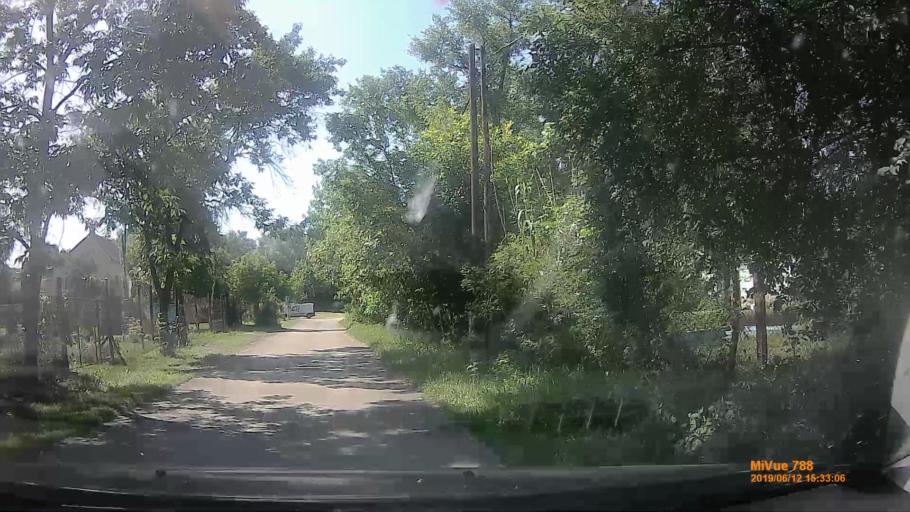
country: HU
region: Csongrad
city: Mako
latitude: 46.1987
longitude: 20.4689
